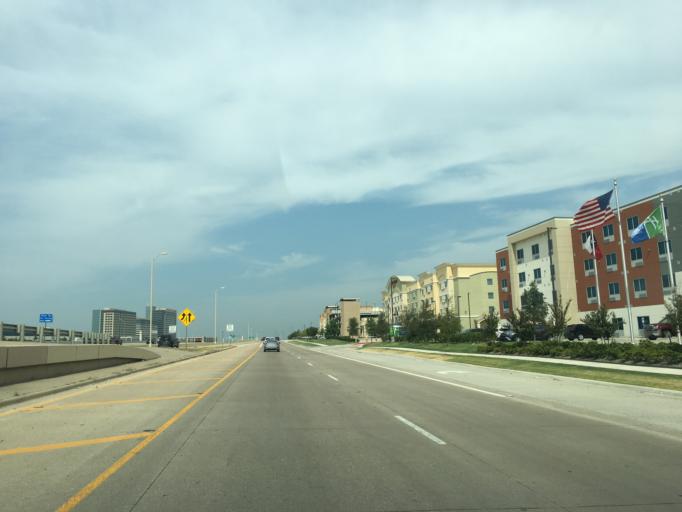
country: US
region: Texas
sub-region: Collin County
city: Plano
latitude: 33.0034
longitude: -96.6857
